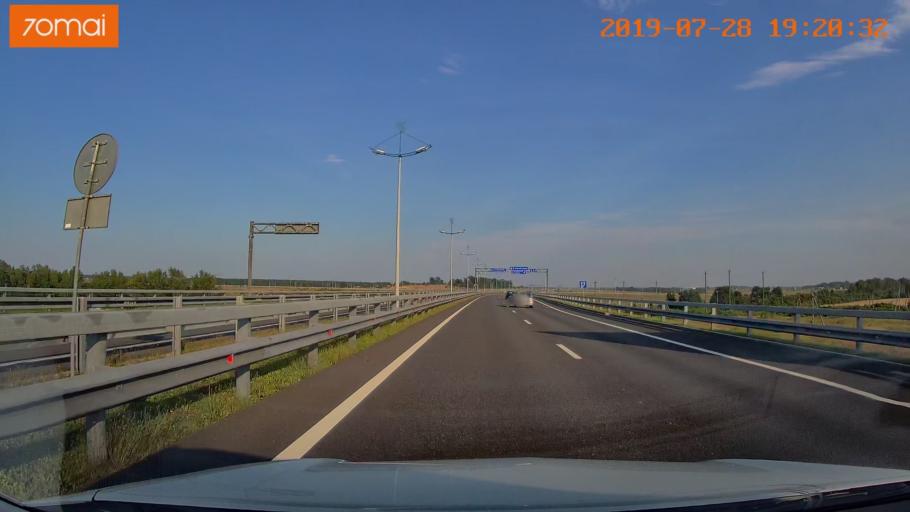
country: RU
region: Kaliningrad
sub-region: Zelenogradskiy Rayon
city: Zelenogradsk
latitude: 54.9144
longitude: 20.4882
